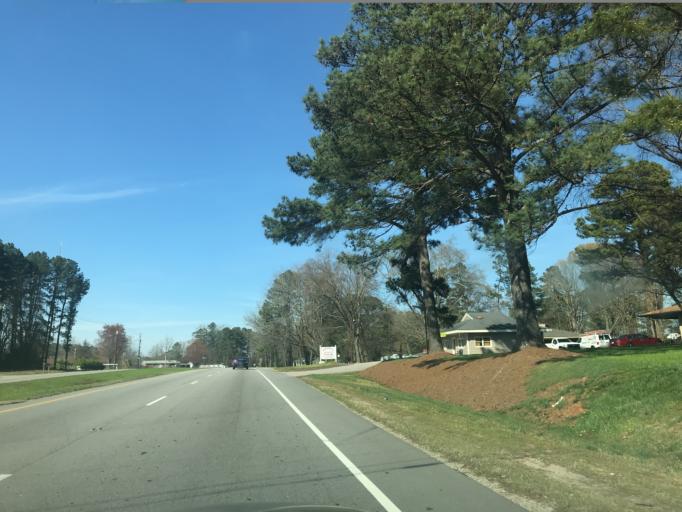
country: US
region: North Carolina
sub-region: Wake County
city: Garner
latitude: 35.6977
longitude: -78.6720
